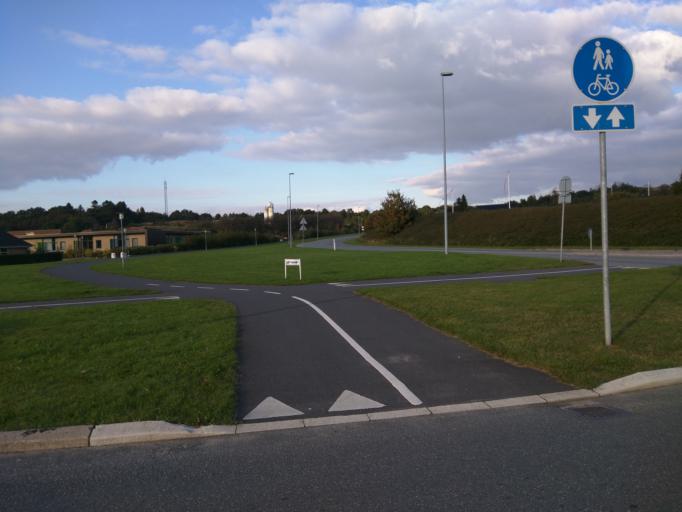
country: DK
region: Central Jutland
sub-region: Viborg Kommune
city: Viborg
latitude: 56.4338
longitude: 9.3779
